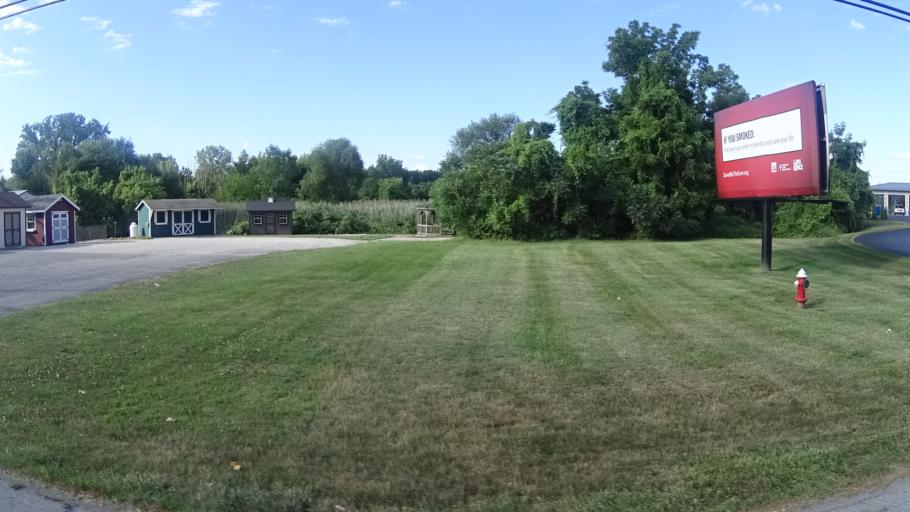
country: US
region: Ohio
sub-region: Erie County
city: Sandusky
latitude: 41.4279
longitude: -82.6654
